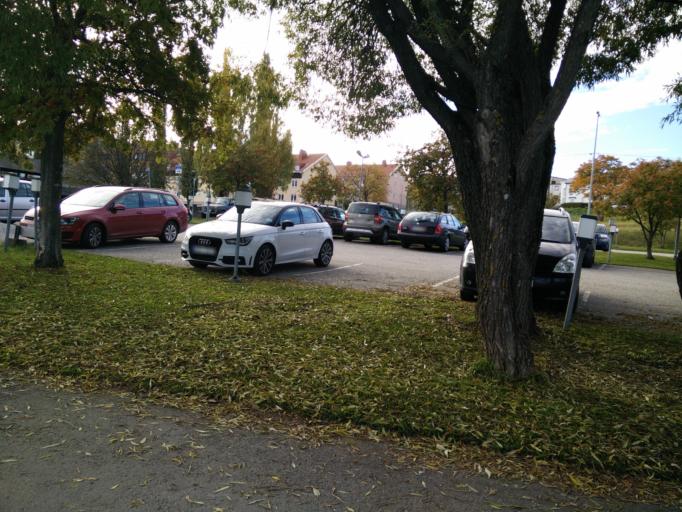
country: SE
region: Vaesternorrland
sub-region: Haernoesands Kommun
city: Haernoesand
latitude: 62.6310
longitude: 17.9316
